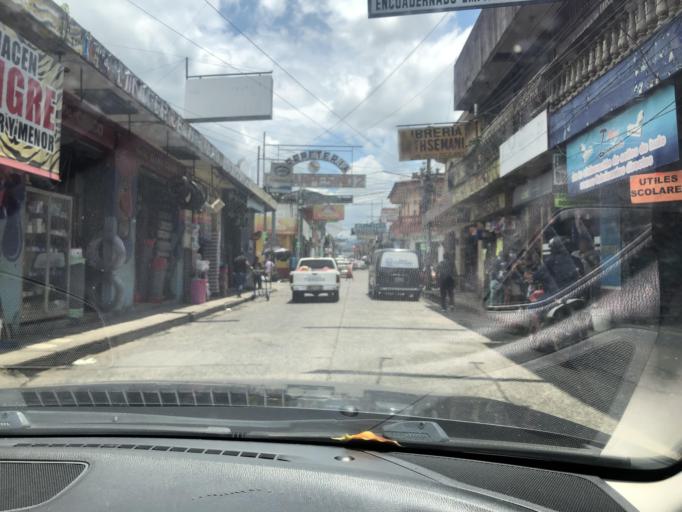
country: GT
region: Quetzaltenango
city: Coatepeque
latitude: 14.7035
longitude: -91.8646
